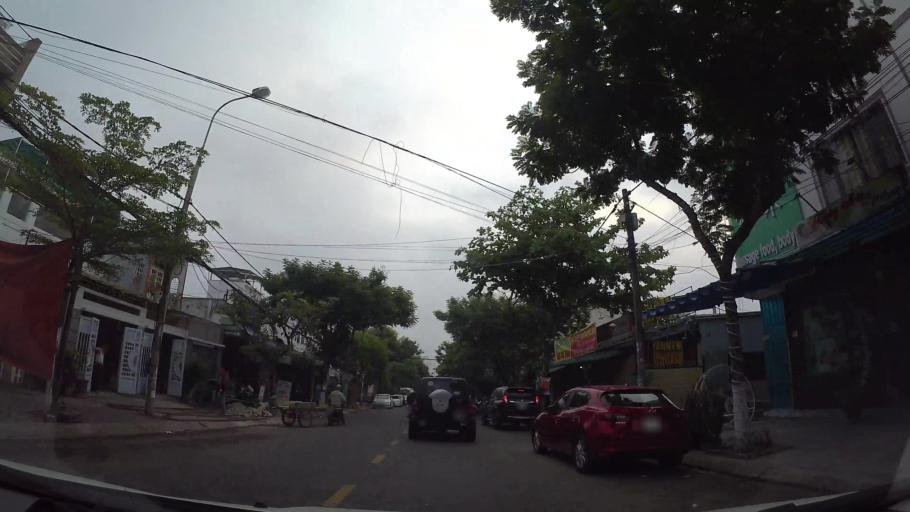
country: VN
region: Da Nang
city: Son Tra
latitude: 16.0497
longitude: 108.2394
